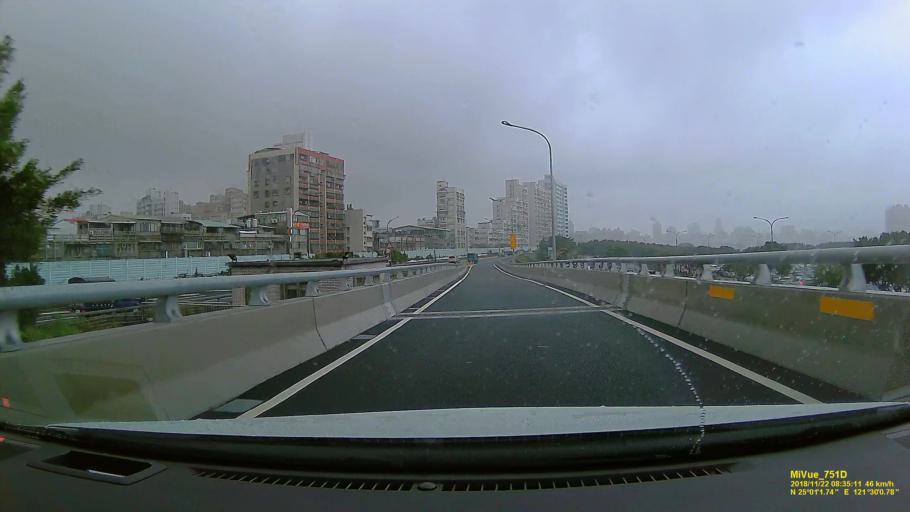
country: TW
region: Taipei
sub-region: Taipei
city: Banqiao
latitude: 25.0172
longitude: 121.5003
